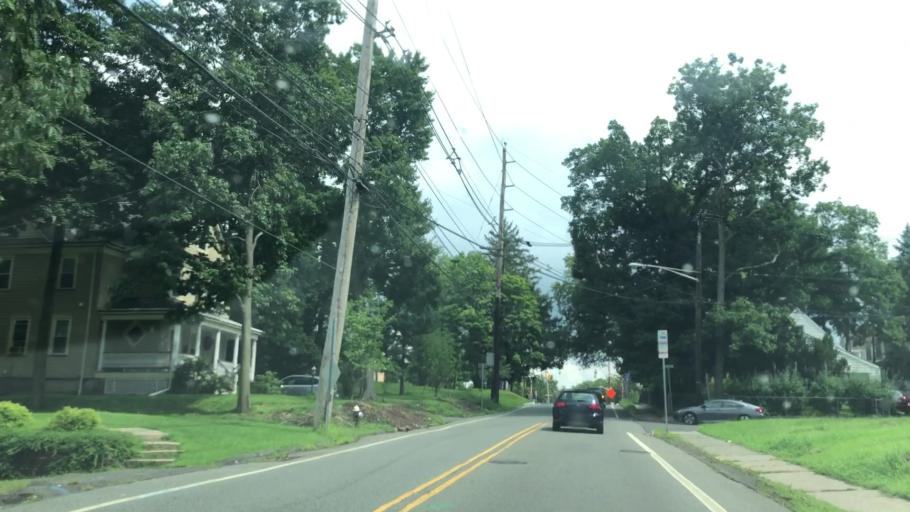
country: US
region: New Jersey
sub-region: Passaic County
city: Little Falls
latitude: 40.8746
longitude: -74.2084
